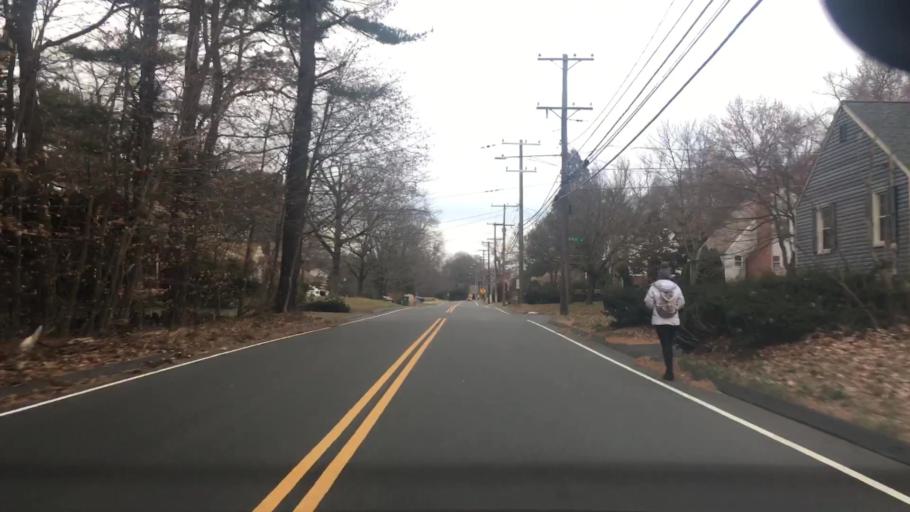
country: US
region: Connecticut
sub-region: Hartford County
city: Plainville
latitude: 41.6652
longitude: -72.9022
